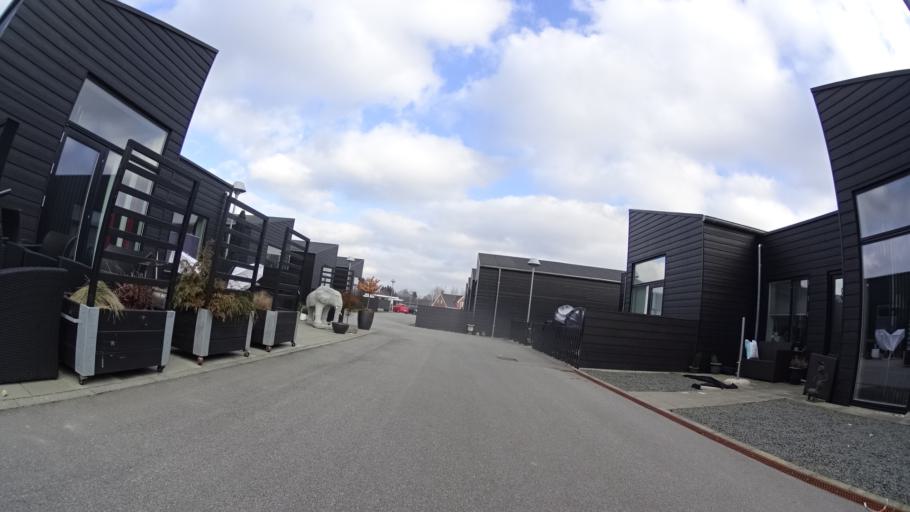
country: DK
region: Central Jutland
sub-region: Arhus Kommune
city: Tranbjerg
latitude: 56.0826
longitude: 10.1168
